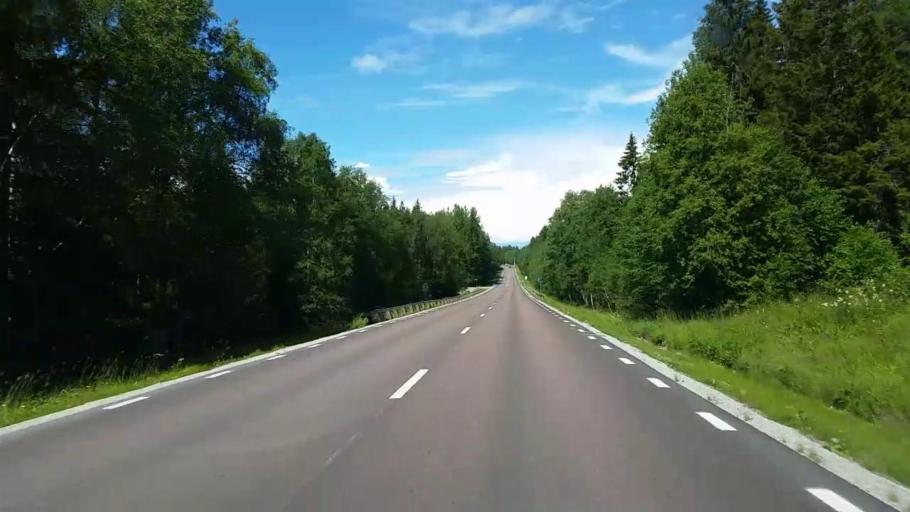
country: SE
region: Dalarna
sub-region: Rattviks Kommun
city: Raettvik
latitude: 61.0293
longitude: 15.2072
